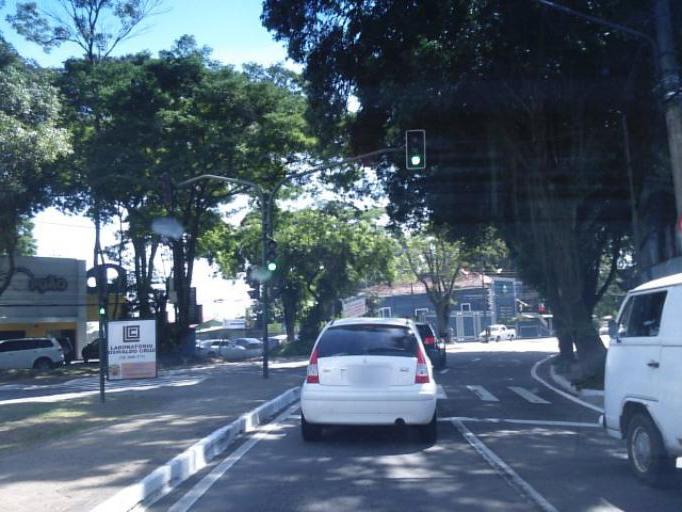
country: BR
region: Sao Paulo
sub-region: Sao Jose Dos Campos
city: Sao Jose dos Campos
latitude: -23.1927
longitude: -45.8931
